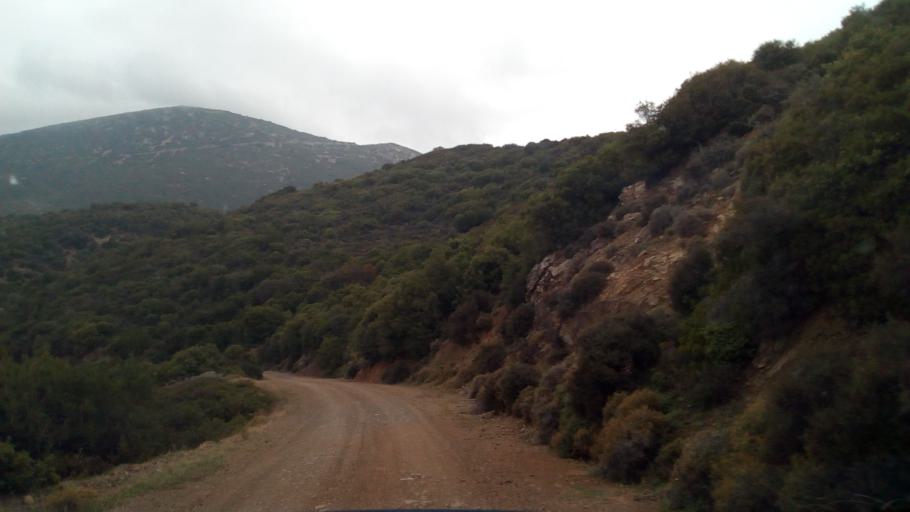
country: GR
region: West Greece
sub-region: Nomos Achaias
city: Aigio
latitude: 38.3734
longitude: 22.1563
